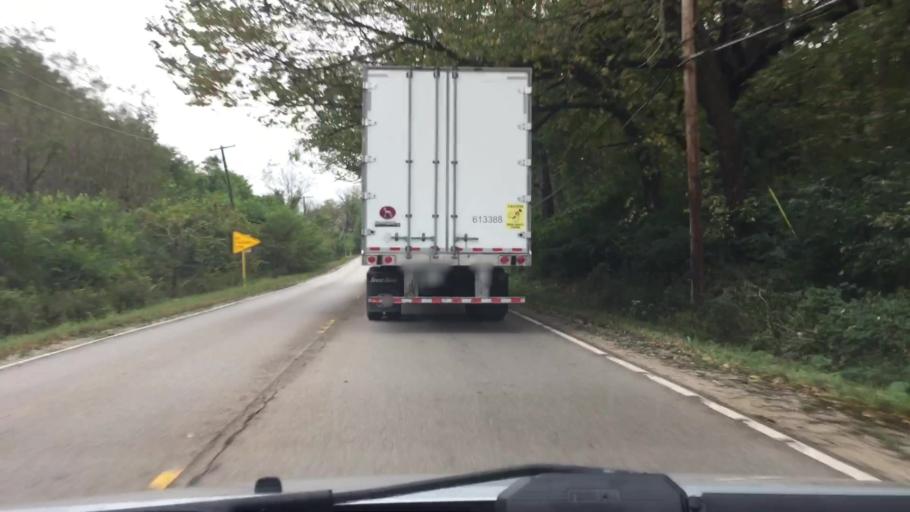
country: US
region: Illinois
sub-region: Kane County
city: Sleepy Hollow
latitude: 42.1191
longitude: -88.2986
